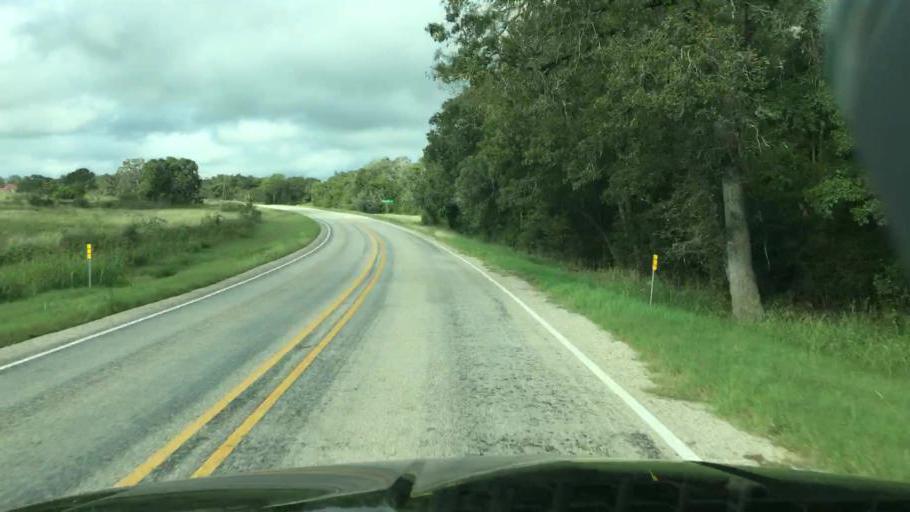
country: US
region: Texas
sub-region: Lee County
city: Giddings
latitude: 30.2716
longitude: -96.8142
